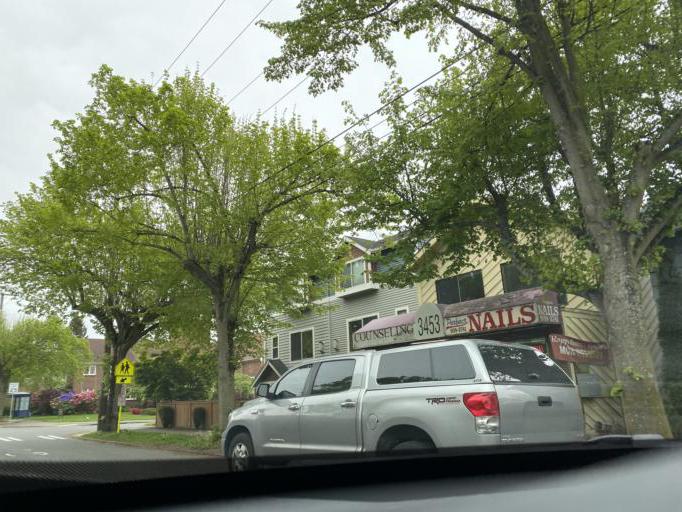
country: US
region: Washington
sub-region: King County
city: White Center
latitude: 47.5724
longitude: -122.3867
